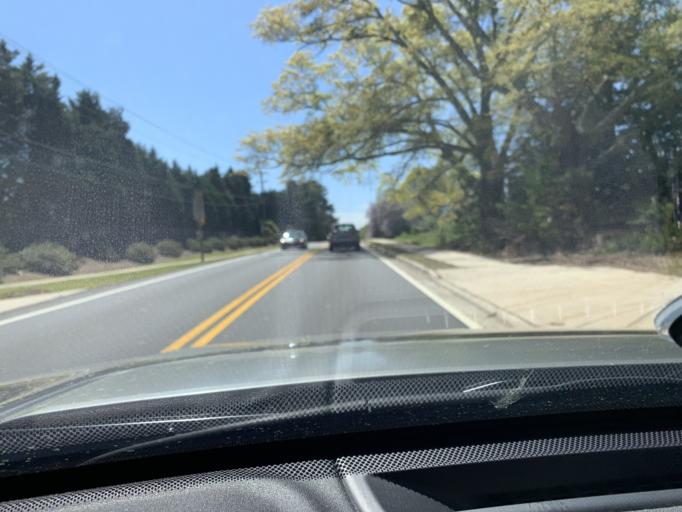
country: US
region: Georgia
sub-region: Fulton County
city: Milton
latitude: 34.1744
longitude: -84.2252
